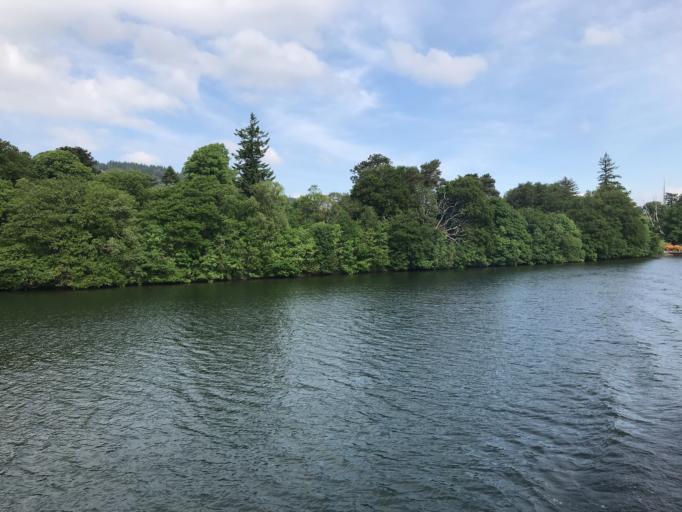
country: GB
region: England
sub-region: Cumbria
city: Windermere
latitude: 54.3585
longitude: -2.9343
